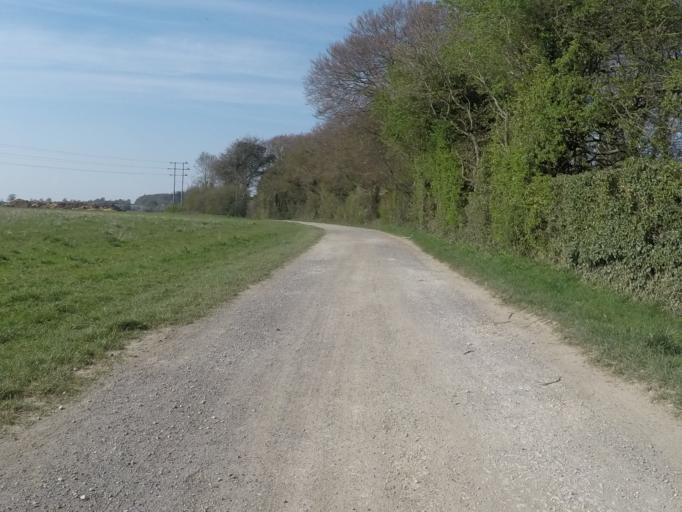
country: GB
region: England
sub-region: Oxfordshire
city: Charlbury
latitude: 51.8828
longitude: -1.4498
